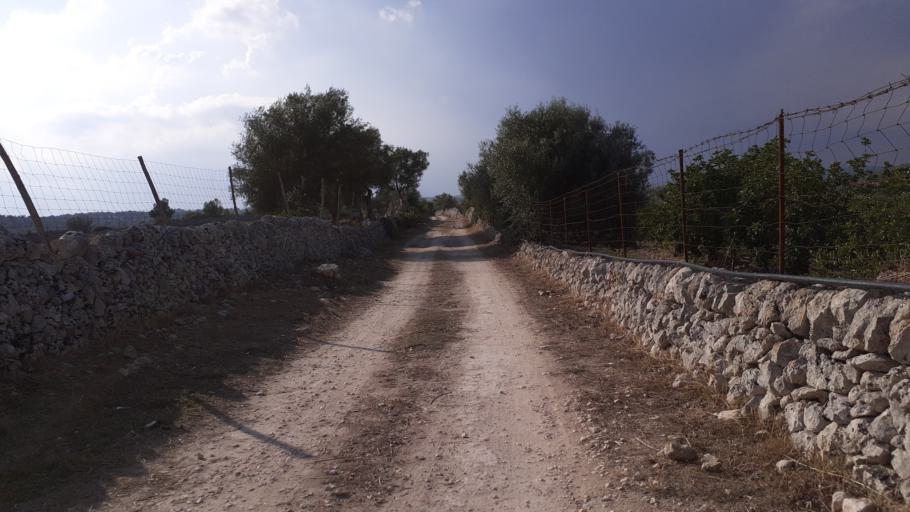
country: IT
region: Sicily
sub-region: Provincia di Siracusa
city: Canicattini Bagni
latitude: 36.9800
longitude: 15.0933
